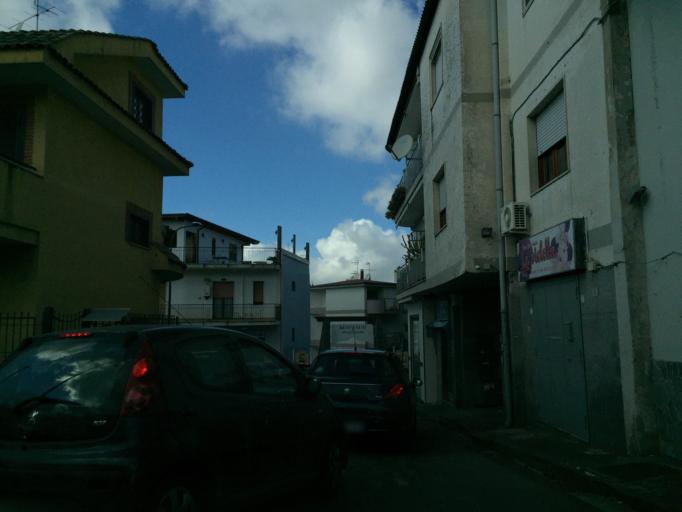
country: IT
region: Campania
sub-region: Provincia di Napoli
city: Massa di Somma
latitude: 40.8453
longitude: 14.3730
